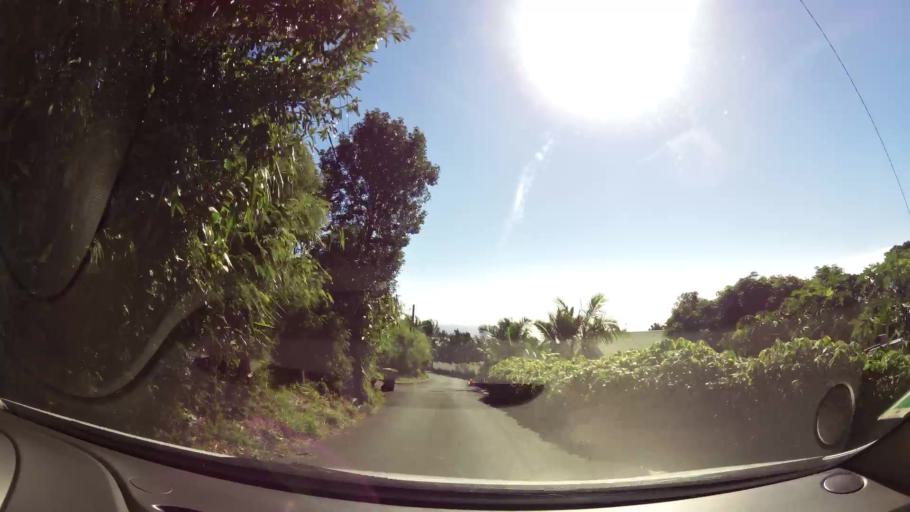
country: RE
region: Reunion
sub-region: Reunion
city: Saint-Denis
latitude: -20.9137
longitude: 55.4819
